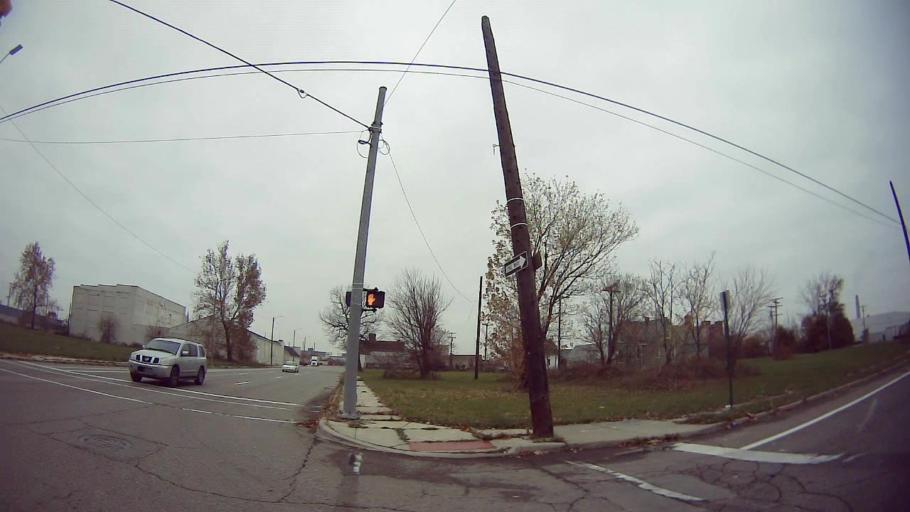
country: US
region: Michigan
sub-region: Wayne County
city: Hamtramck
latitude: 42.3624
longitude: -83.0430
